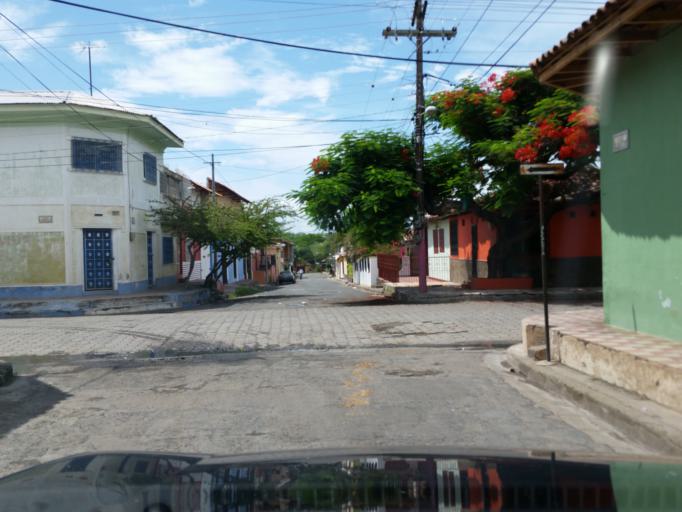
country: NI
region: Granada
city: Granada
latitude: 11.9326
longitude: -85.9504
